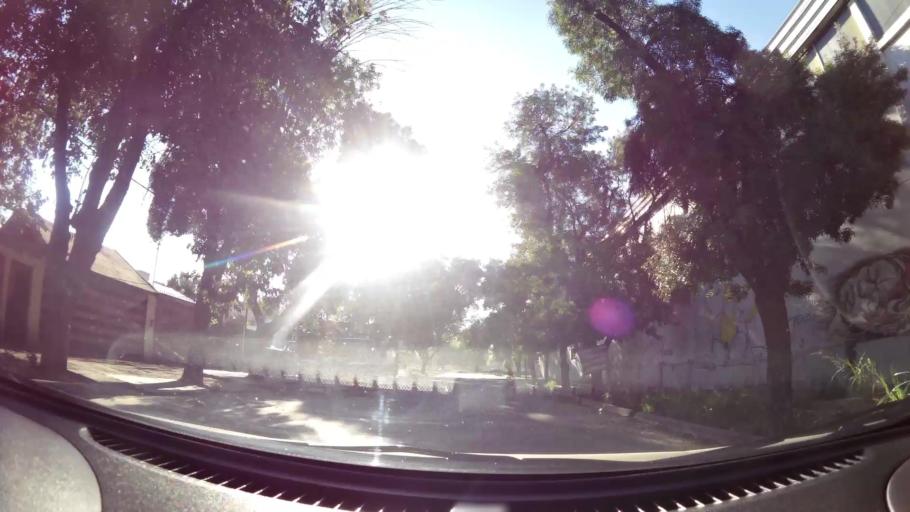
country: AR
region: Mendoza
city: Mendoza
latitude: -32.8736
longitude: -68.8215
